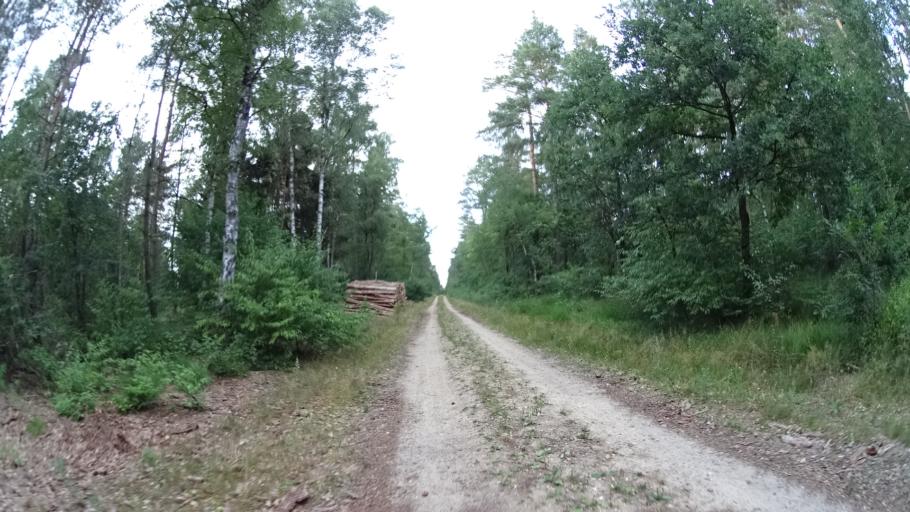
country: DE
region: Lower Saxony
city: Handeloh
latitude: 53.2038
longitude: 9.8797
